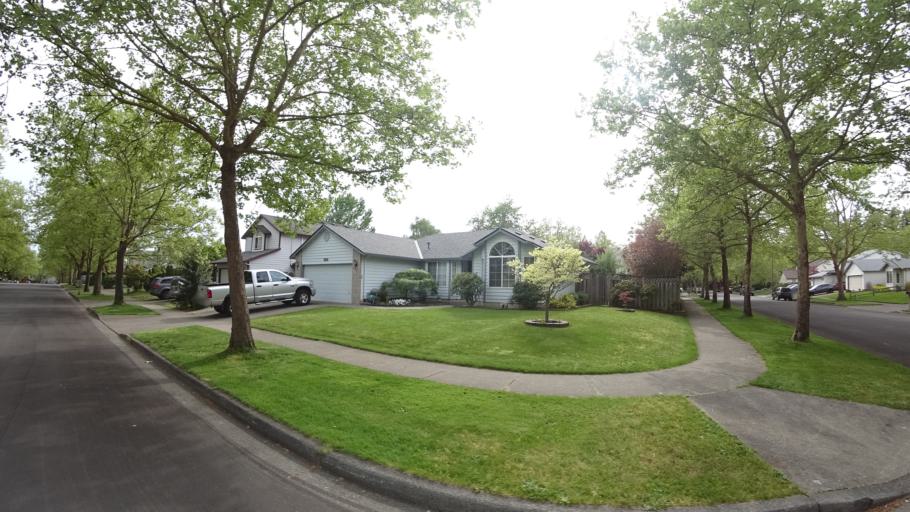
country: US
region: Oregon
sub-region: Washington County
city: Aloha
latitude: 45.5119
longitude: -122.9233
